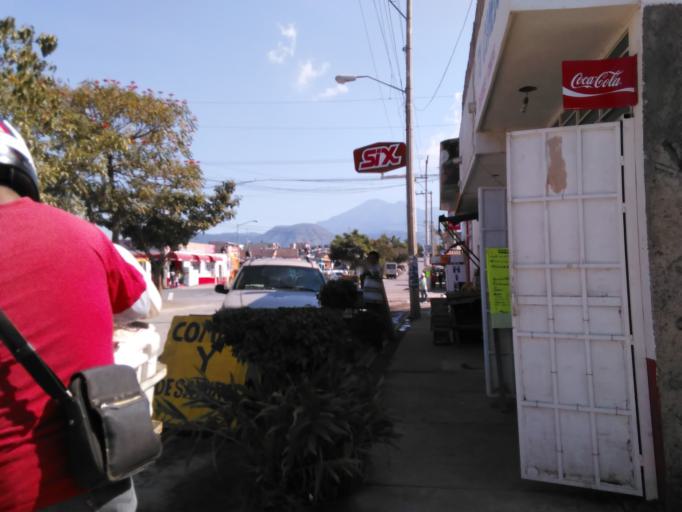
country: MX
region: Nayarit
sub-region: Tepic
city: La Corregidora
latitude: 21.4883
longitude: -104.8296
